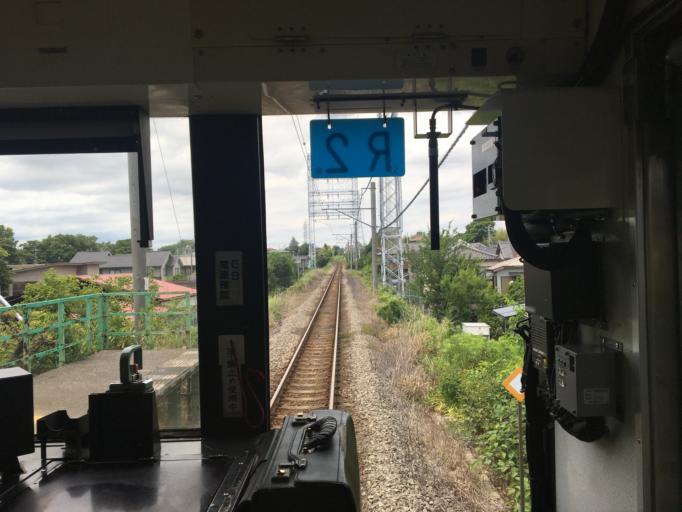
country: JP
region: Kanagawa
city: Zama
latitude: 35.5186
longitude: 139.3808
